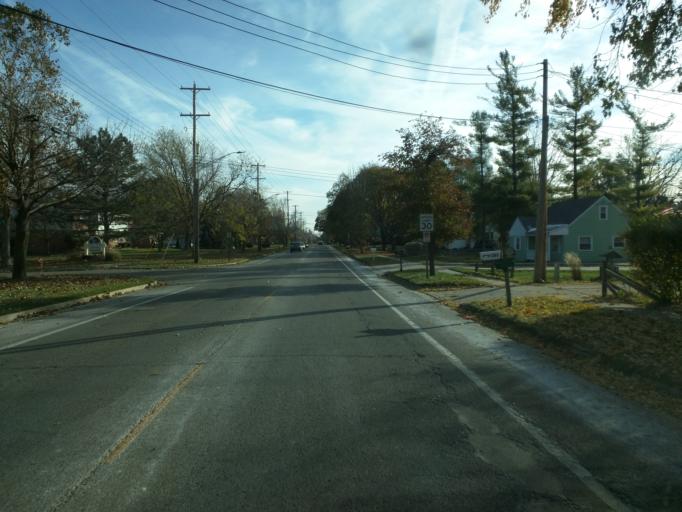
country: US
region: Michigan
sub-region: Ingham County
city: Holt
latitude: 42.6692
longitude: -84.5704
